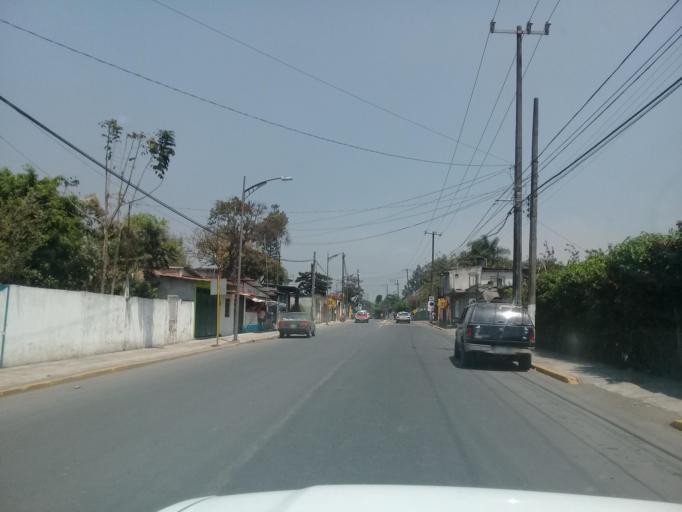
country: MX
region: Veracruz
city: Ixtac Zoquitlan
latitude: 18.8688
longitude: -97.0599
